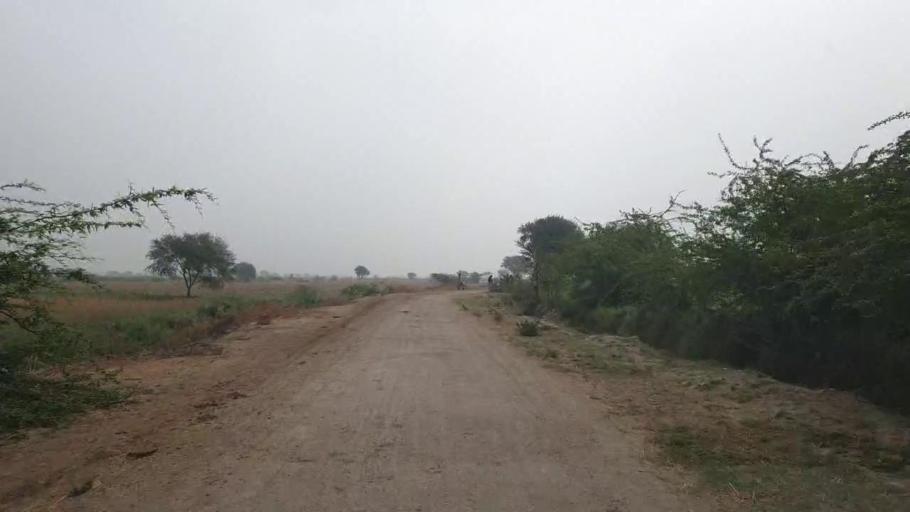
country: PK
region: Sindh
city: Badin
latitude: 24.5855
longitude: 68.6806
